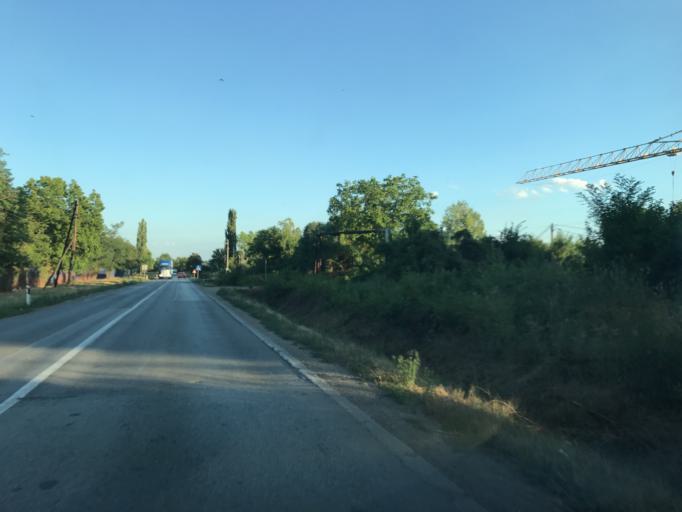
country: RS
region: Central Serbia
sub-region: Podunavski Okrug
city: Smederevo
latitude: 44.6019
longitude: 20.9631
